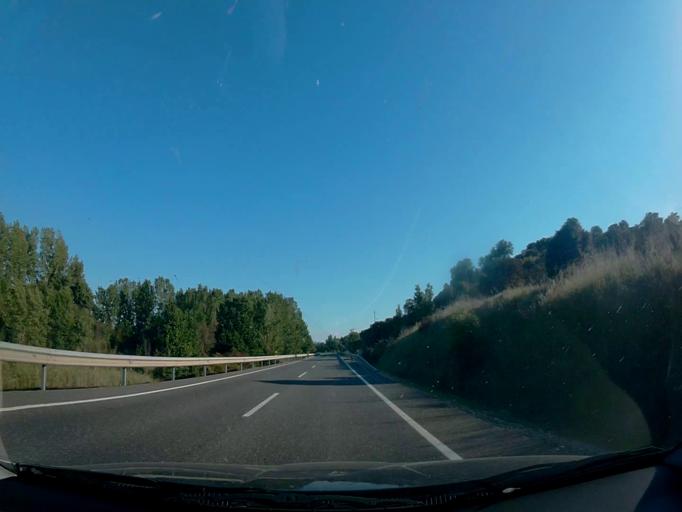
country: ES
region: Castille-La Mancha
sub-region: Province of Toledo
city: Escalona
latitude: 40.1782
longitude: -4.3994
